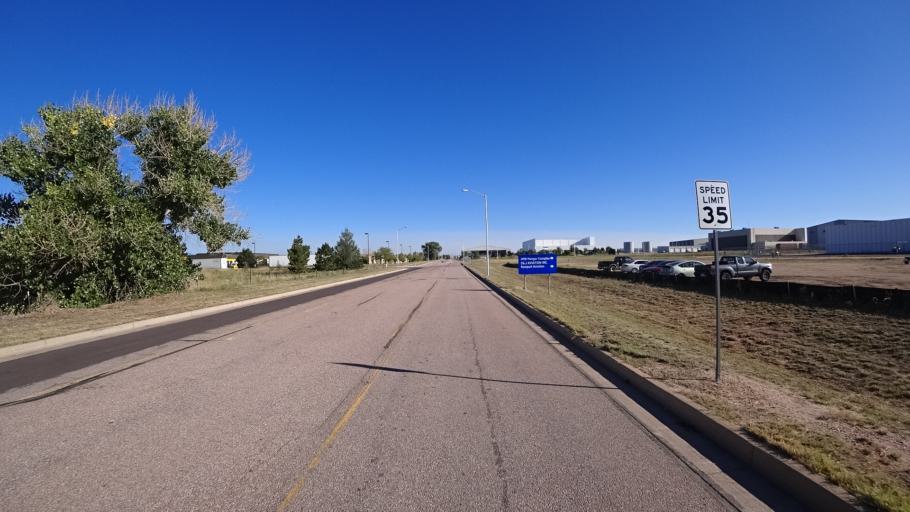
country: US
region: Colorado
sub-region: El Paso County
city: Security-Widefield
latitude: 38.8012
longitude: -104.7235
